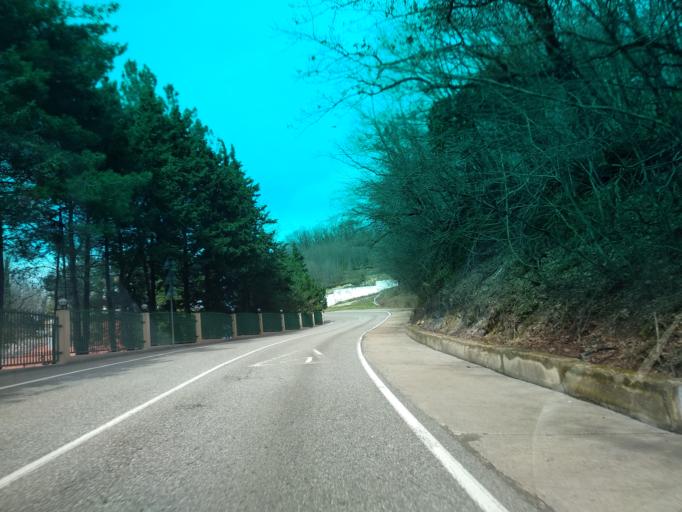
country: RU
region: Krasnodarskiy
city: Shepsi
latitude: 44.0492
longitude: 39.1313
